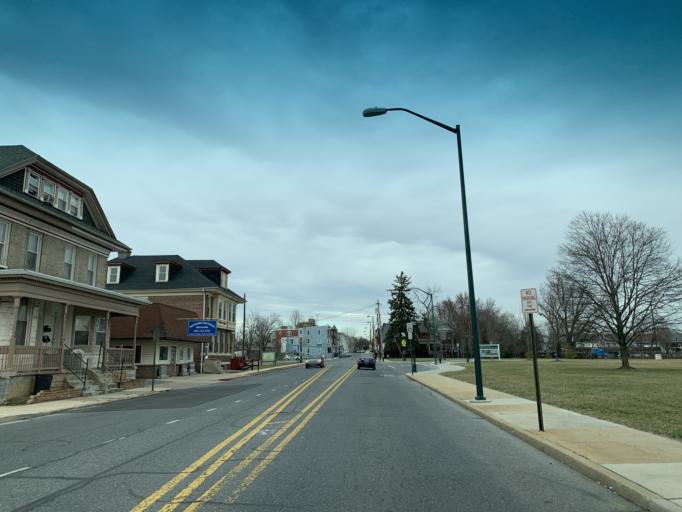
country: US
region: Maryland
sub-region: Washington County
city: Hagerstown
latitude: 39.6326
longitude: -77.7229
